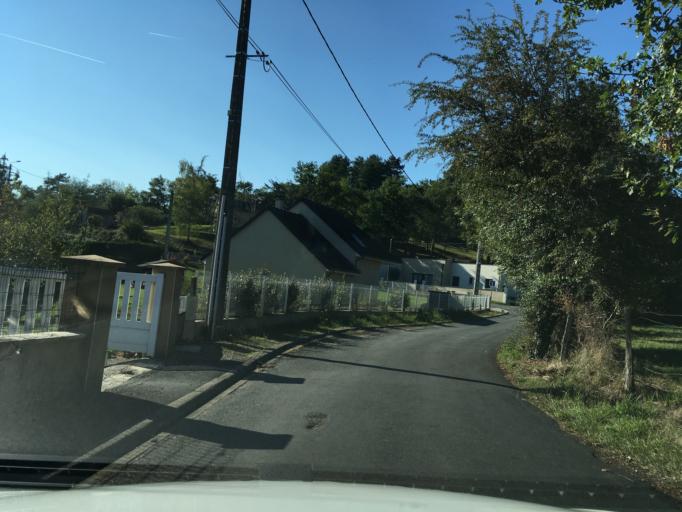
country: FR
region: Limousin
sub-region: Departement de la Correze
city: Malemort-sur-Correze
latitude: 45.1805
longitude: 1.5413
